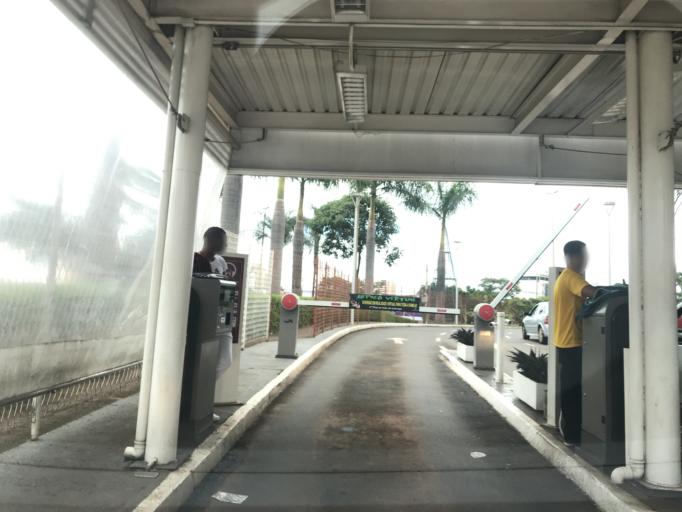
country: BR
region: Federal District
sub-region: Brasilia
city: Brasilia
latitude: -15.8424
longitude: -48.0446
